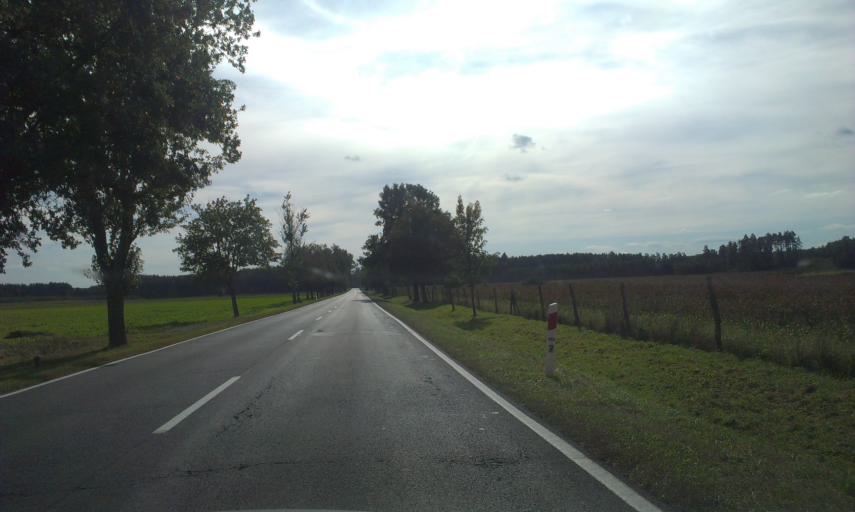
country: PL
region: Greater Poland Voivodeship
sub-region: Powiat zlotowski
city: Okonek
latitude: 53.5583
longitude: 16.8355
